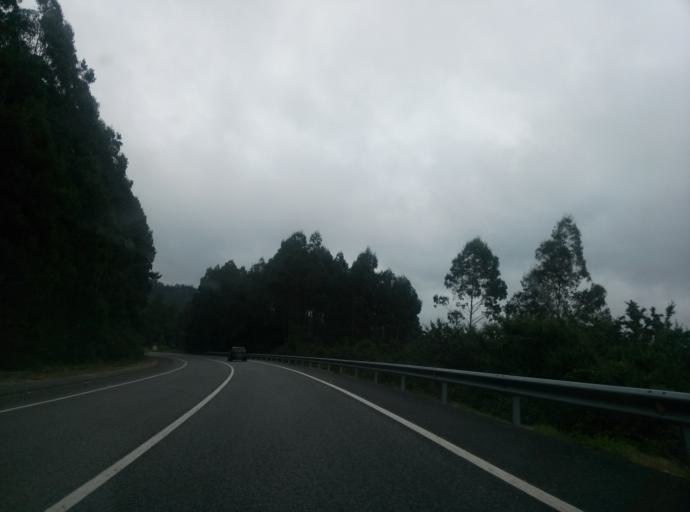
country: ES
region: Galicia
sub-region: Provincia de Lugo
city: Viveiro
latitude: 43.5608
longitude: -7.6432
